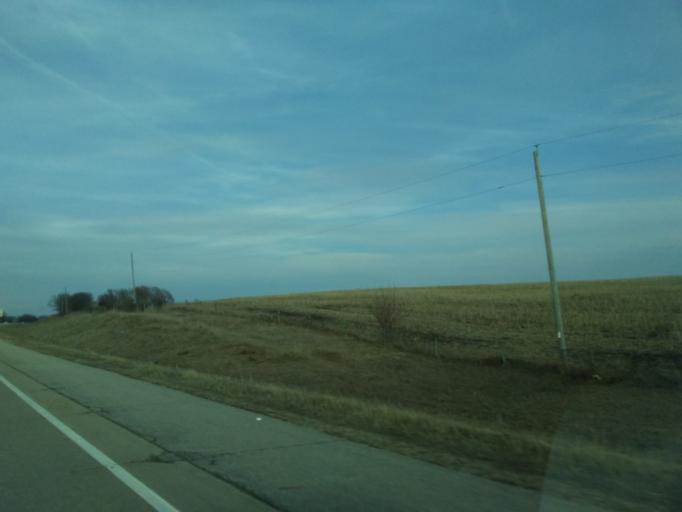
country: US
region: Wisconsin
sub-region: Iowa County
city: Dodgeville
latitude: 42.9701
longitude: -90.0439
